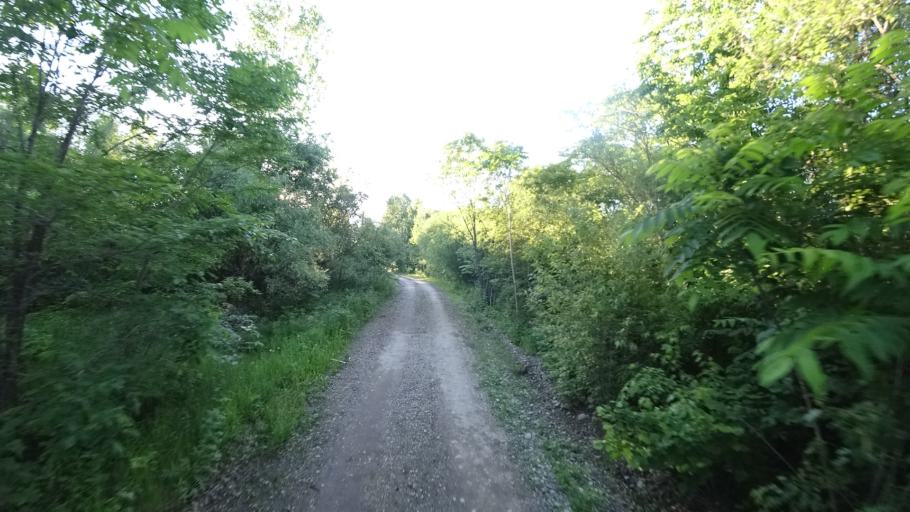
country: RU
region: Khabarovsk Krai
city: Khor
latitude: 47.8538
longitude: 135.0044
